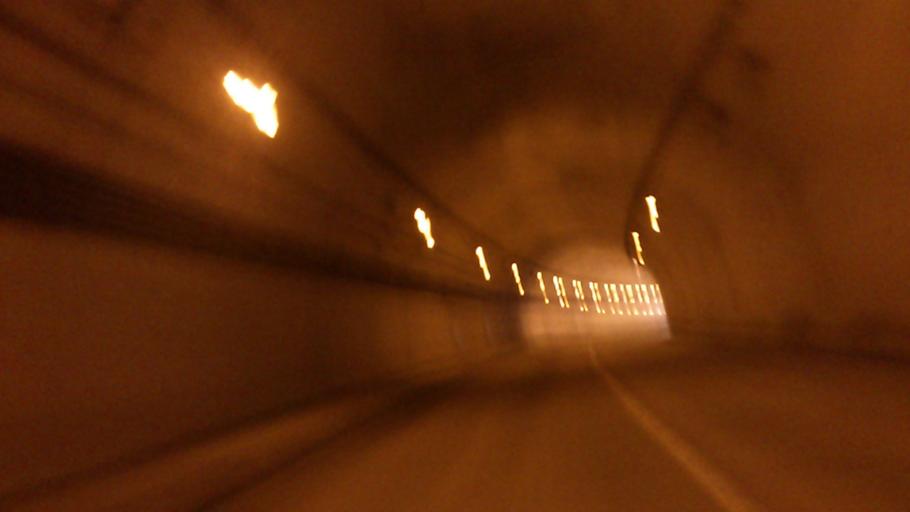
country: JP
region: Hokkaido
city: Kamiiso
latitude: 41.4074
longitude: 140.2088
